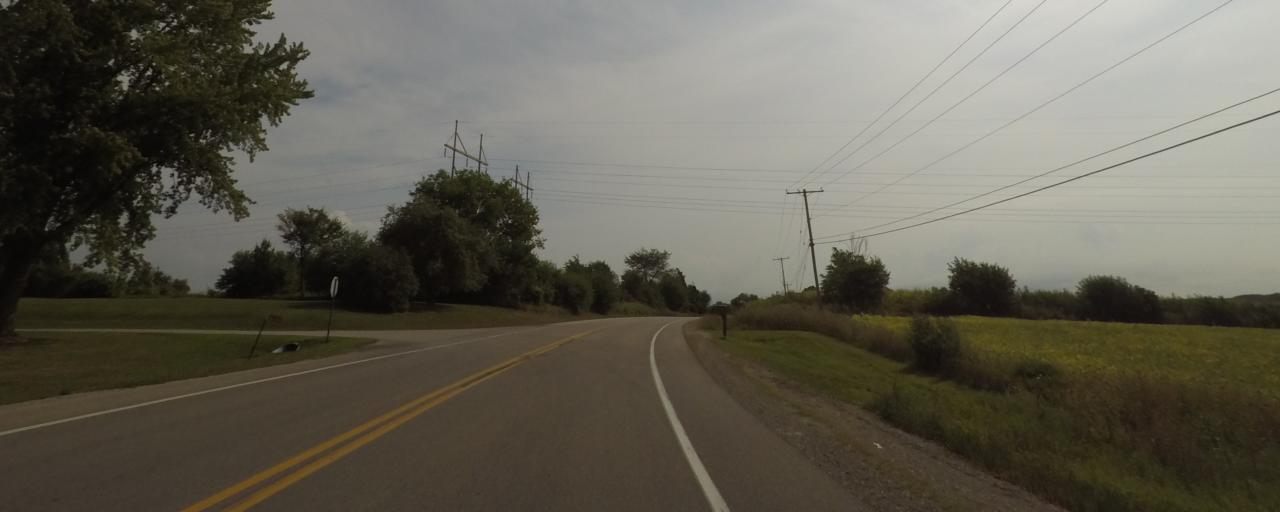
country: US
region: Wisconsin
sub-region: Jefferson County
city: Jefferson
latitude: 42.9853
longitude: -88.8668
